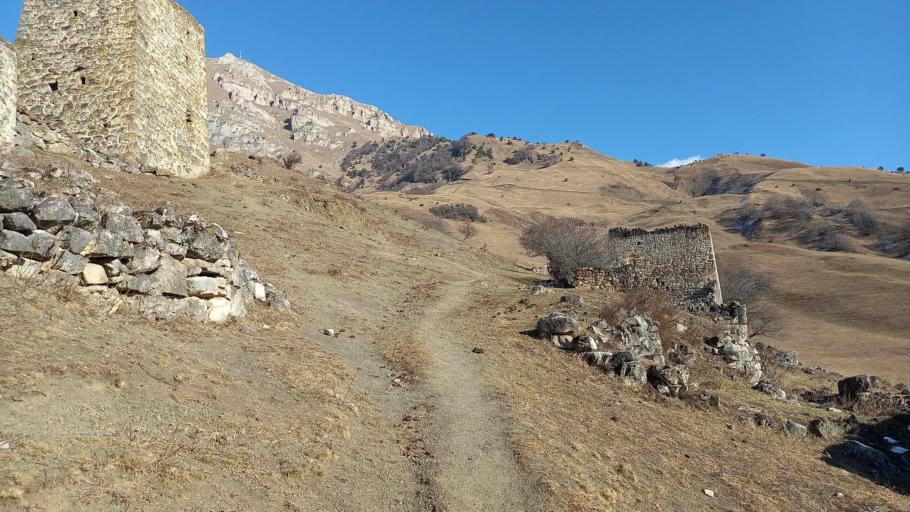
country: RU
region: Ingushetiya
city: Dzhayrakh
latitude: 42.8369
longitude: 44.7215
